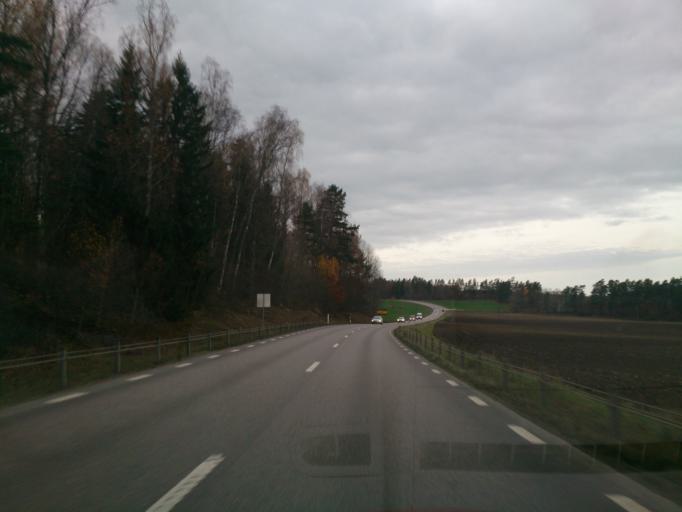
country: SE
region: OEstergoetland
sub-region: Atvidabergs Kommun
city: Atvidaberg
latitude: 58.2547
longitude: 15.9298
